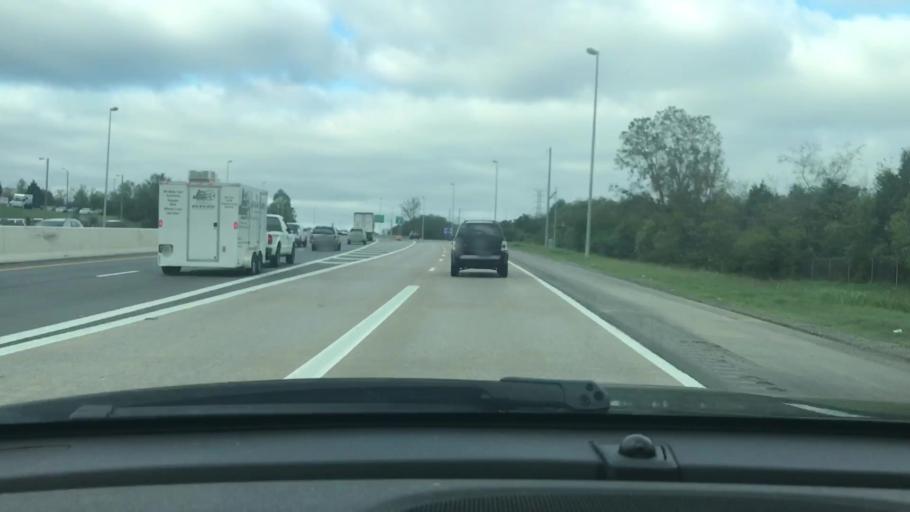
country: US
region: Tennessee
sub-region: Davidson County
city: Goodlettsville
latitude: 36.3115
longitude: -86.6841
